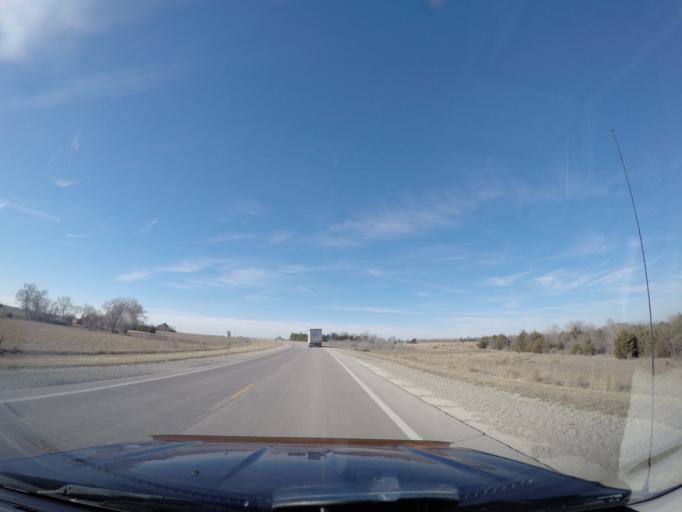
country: US
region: Kansas
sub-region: Marion County
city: Marion
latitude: 38.3606
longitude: -97.1100
